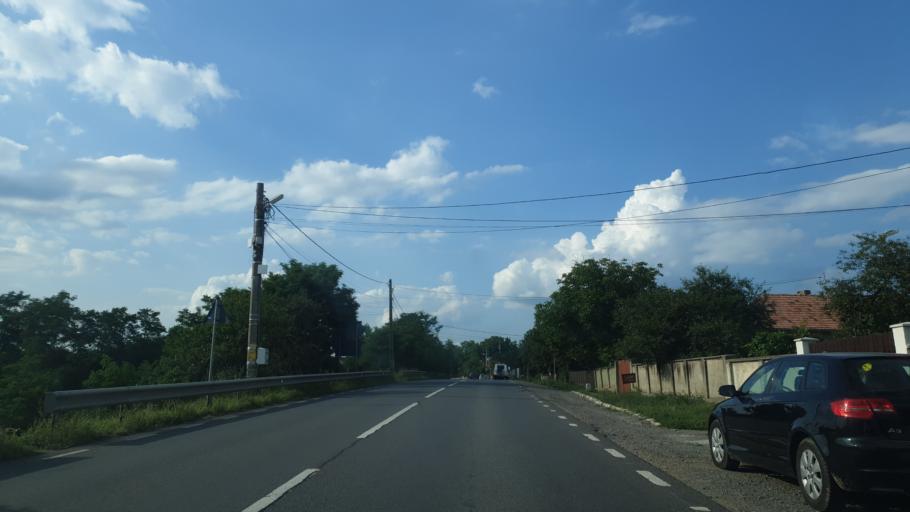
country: RO
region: Covasna
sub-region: Comuna Chichis
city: Chichis
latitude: 45.8096
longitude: 25.8003
